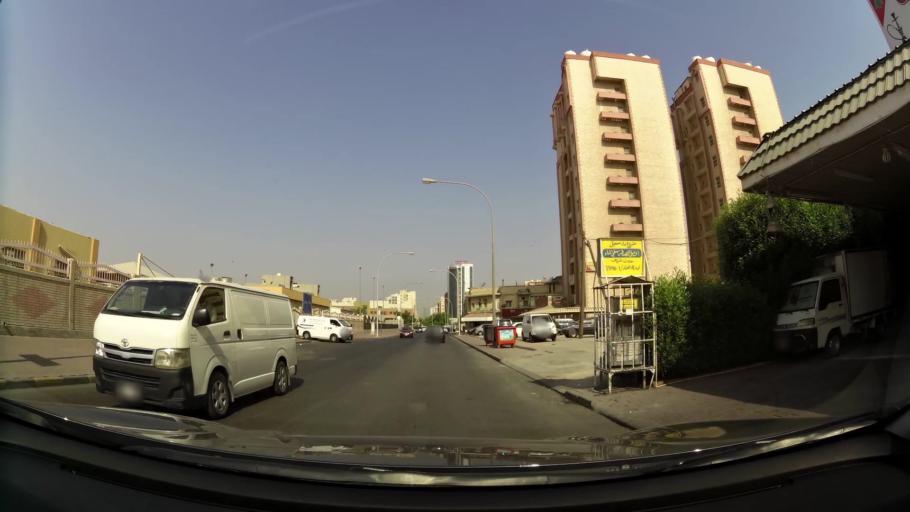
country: KW
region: Muhafazat Hawalli
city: Hawalli
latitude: 29.3324
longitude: 48.0150
